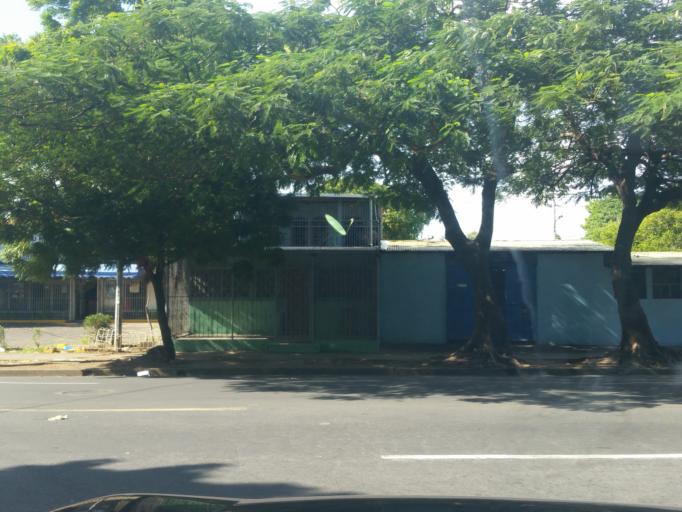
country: NI
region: Managua
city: Managua
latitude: 12.1440
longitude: -86.2657
